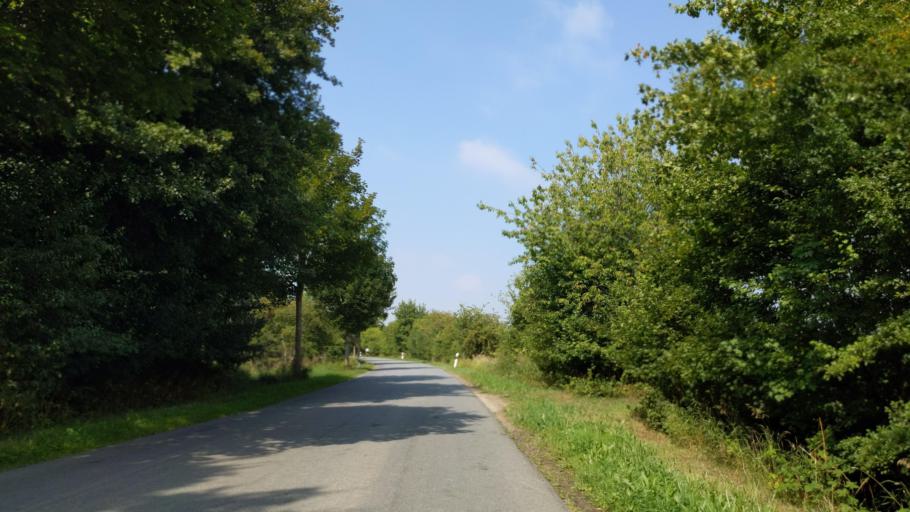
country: DE
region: Schleswig-Holstein
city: Monkhagen
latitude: 53.9199
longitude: 10.5851
